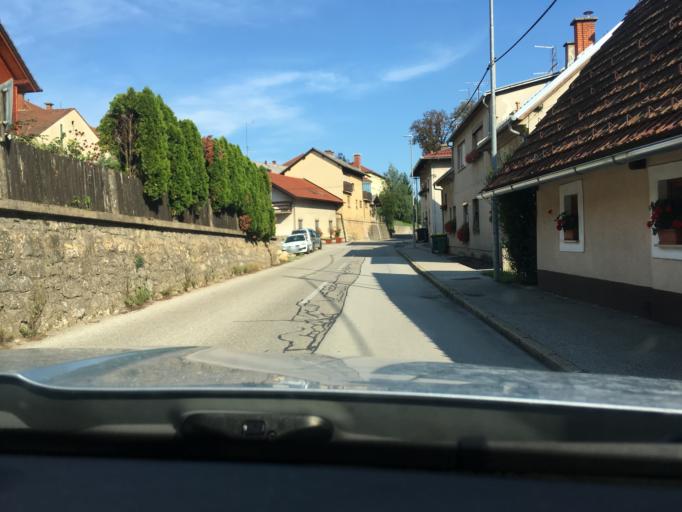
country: SI
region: Crnomelj
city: Crnomelj
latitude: 45.5740
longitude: 15.1896
